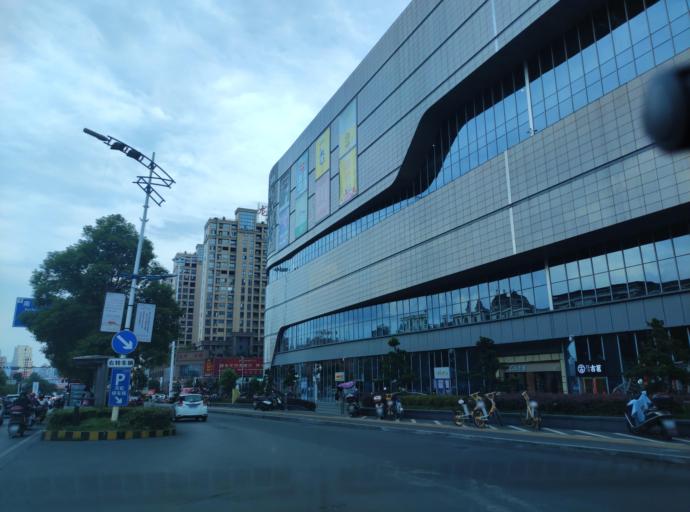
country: CN
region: Jiangxi Sheng
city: Pingxiang
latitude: 27.6345
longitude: 113.8693
